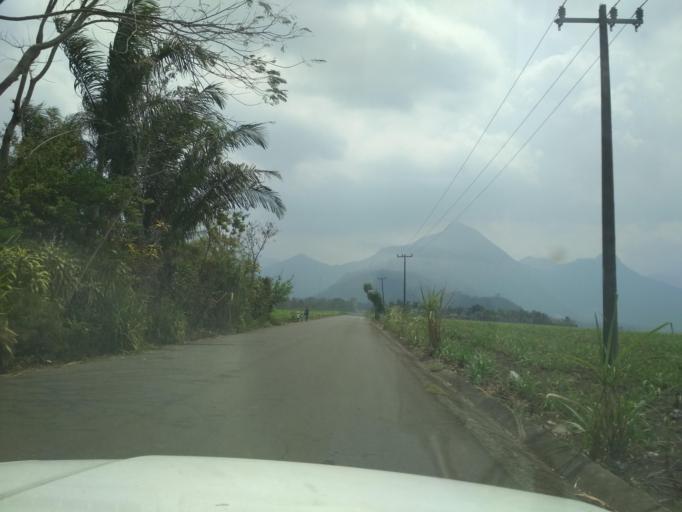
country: MX
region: Veracruz
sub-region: Cordoba
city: San Jose de Tapia
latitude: 18.8457
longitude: -96.9801
